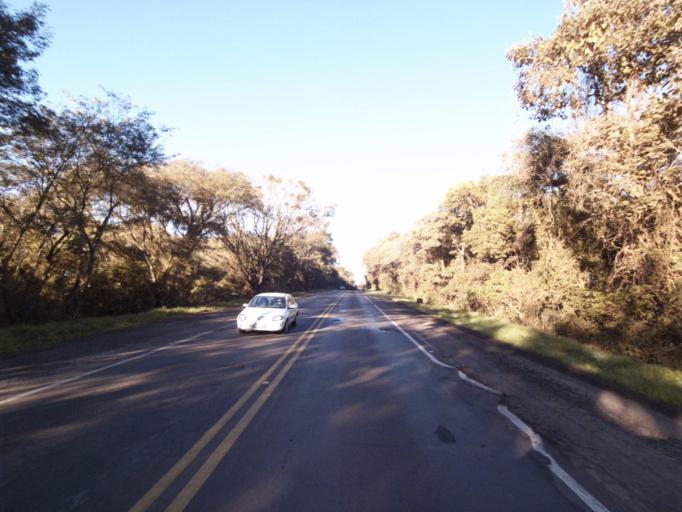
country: BR
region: Santa Catarina
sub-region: Sao Lourenco Do Oeste
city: Sao Lourenco dOeste
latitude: -26.7716
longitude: -53.2696
